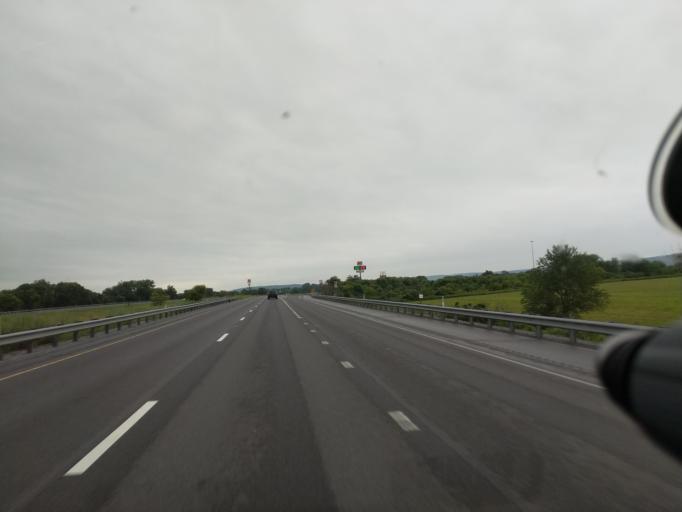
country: US
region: Pennsylvania
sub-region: Clinton County
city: Mill Hall
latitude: 41.0338
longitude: -77.5102
